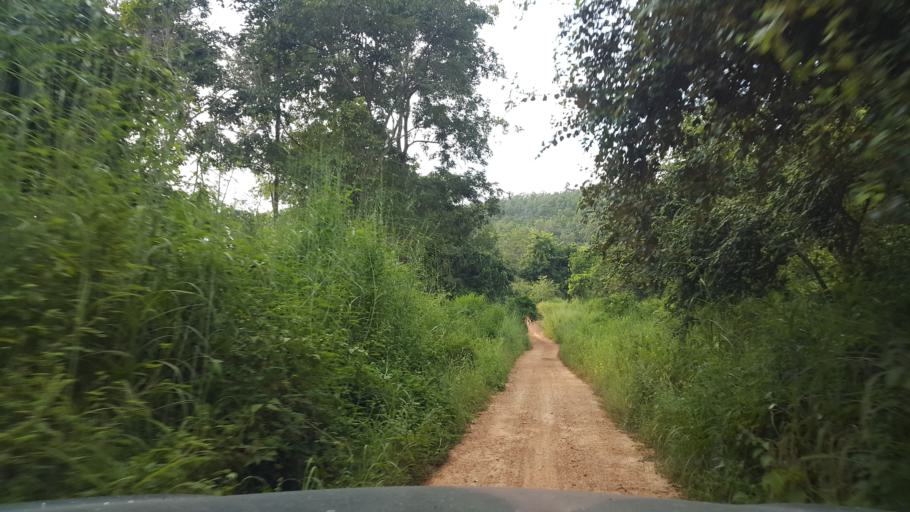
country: TH
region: Chiang Mai
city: San Sai
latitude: 18.9240
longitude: 99.0822
